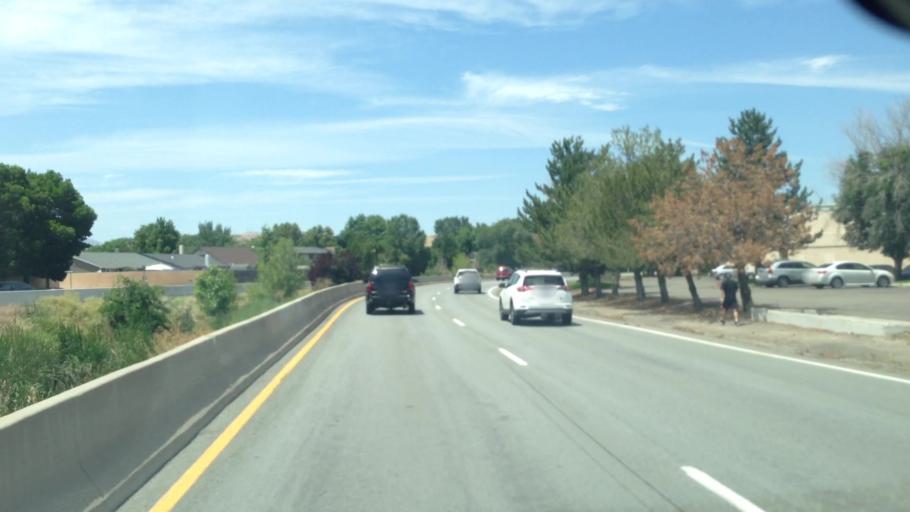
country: US
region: Nevada
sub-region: Washoe County
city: Sparks
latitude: 39.5541
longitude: -119.7228
